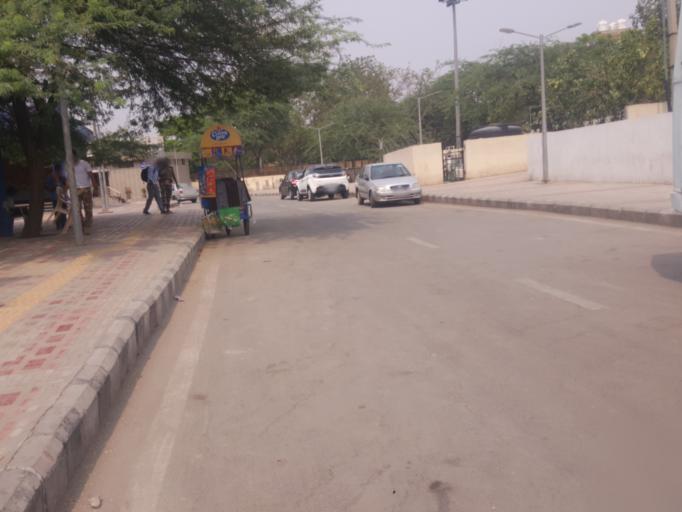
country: IN
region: NCT
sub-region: Central Delhi
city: Karol Bagh
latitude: 28.5659
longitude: 77.1225
